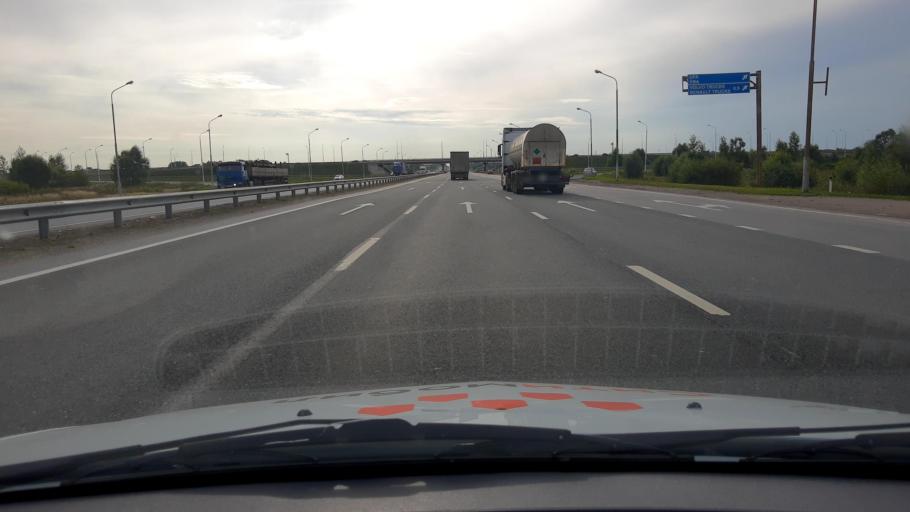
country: RU
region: Bashkortostan
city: Kabakovo
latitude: 54.6517
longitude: 56.0892
